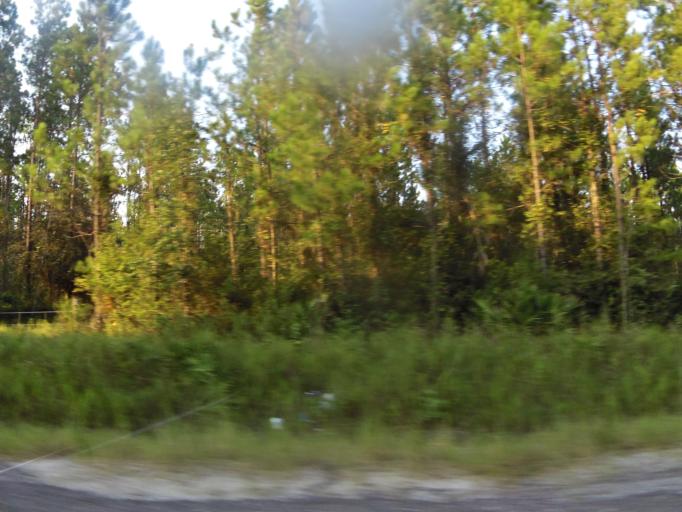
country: US
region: Florida
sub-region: Duval County
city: Baldwin
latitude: 30.3877
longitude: -82.0490
